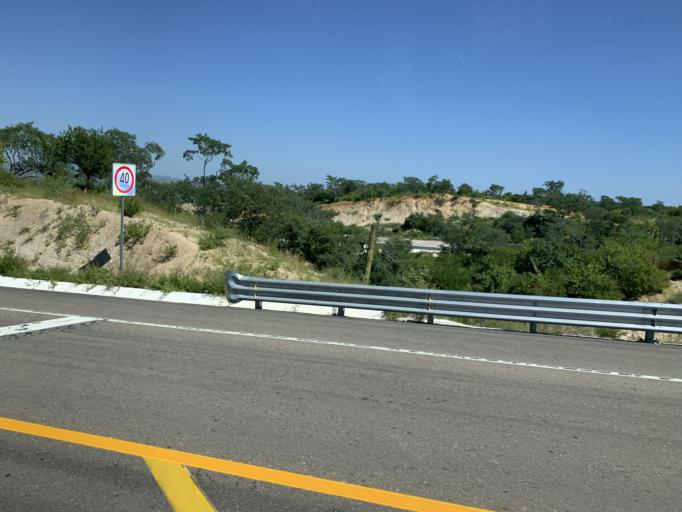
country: MX
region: Baja California Sur
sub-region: Los Cabos
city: San Jose del Cabo
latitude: 23.0724
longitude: -109.7480
